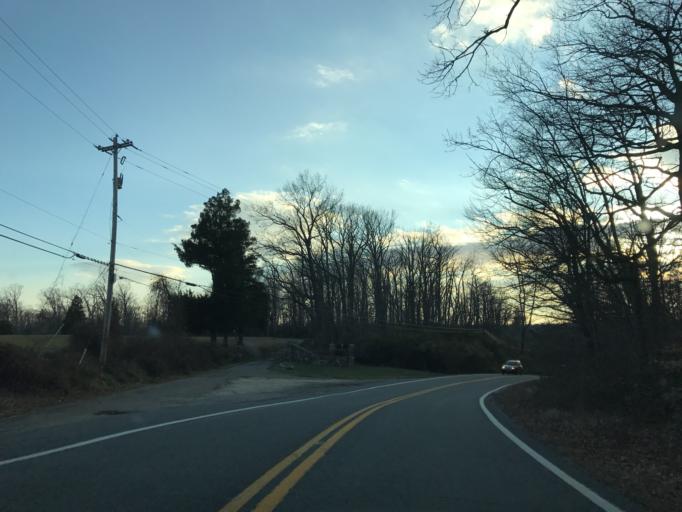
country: US
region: Maryland
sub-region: Cecil County
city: Charlestown
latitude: 39.5033
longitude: -75.9602
